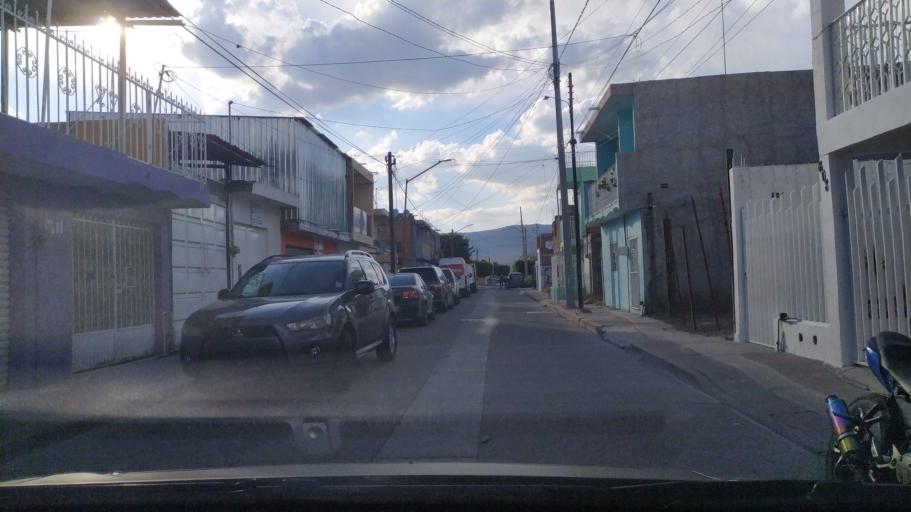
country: MX
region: Guanajuato
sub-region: Purisima del Rincon
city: Monte Grande
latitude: 21.0079
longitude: -101.8585
